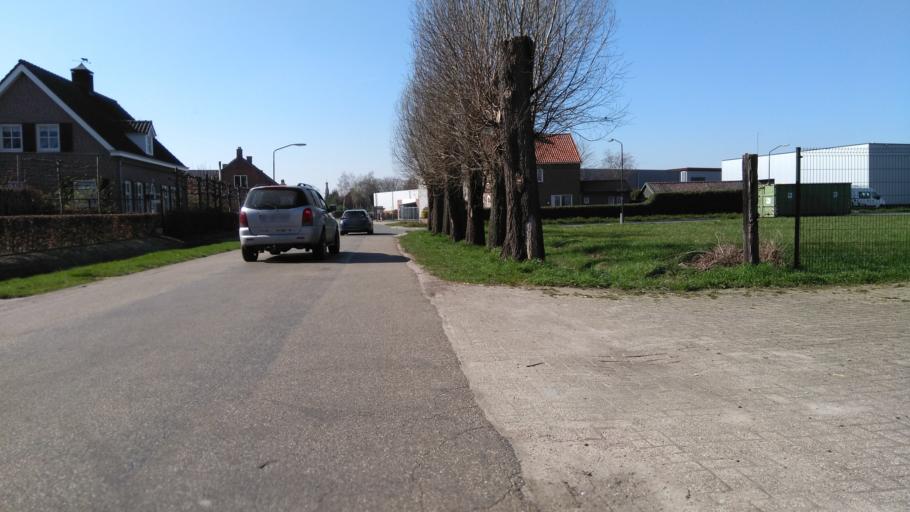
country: NL
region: North Brabant
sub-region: Gemeente Baarle-Nassau
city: Baarle-Nassau
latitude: 51.4416
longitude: 4.9435
